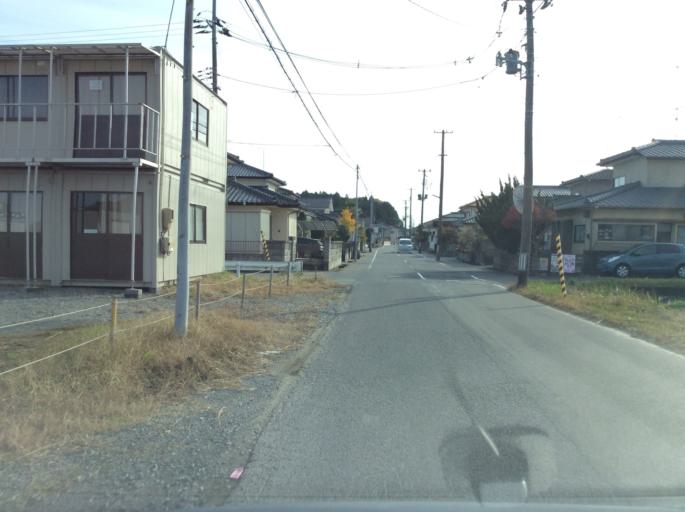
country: JP
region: Fukushima
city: Iwaki
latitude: 37.0739
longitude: 140.9426
